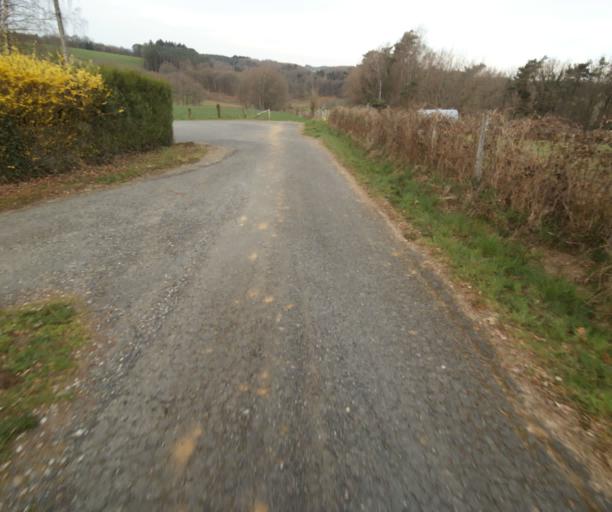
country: FR
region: Limousin
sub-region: Departement de la Correze
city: Correze
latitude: 45.4266
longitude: 1.8291
